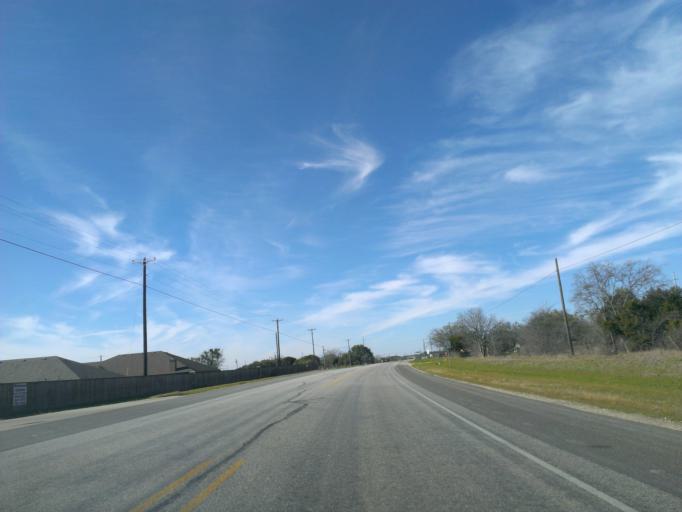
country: US
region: Texas
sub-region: Bell County
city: Nolanville
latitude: 31.0897
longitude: -97.6084
